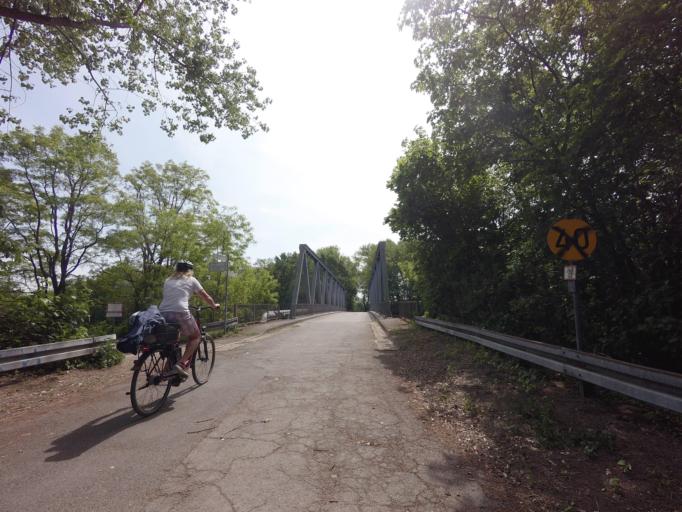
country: DE
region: Lower Saxony
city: Klein Schwulper
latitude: 52.3138
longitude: 10.4722
